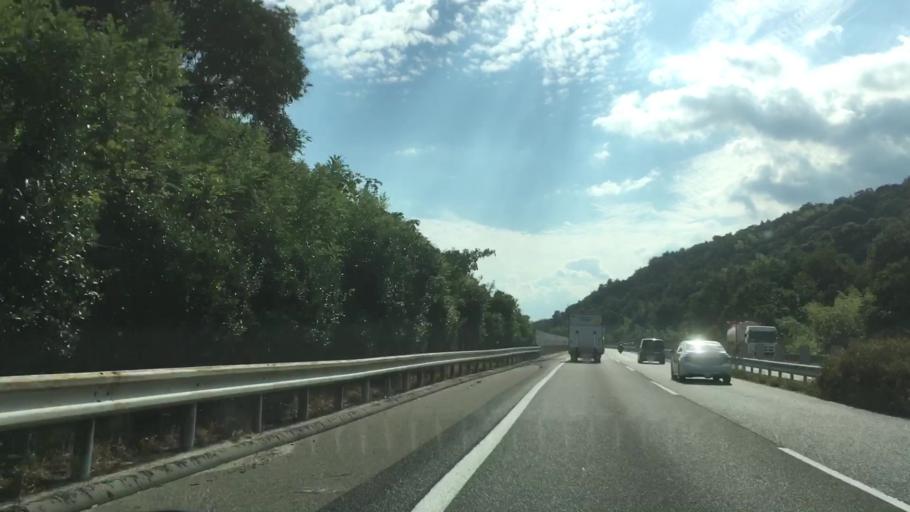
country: JP
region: Hiroshima
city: Ono-hara
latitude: 34.2867
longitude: 132.2641
